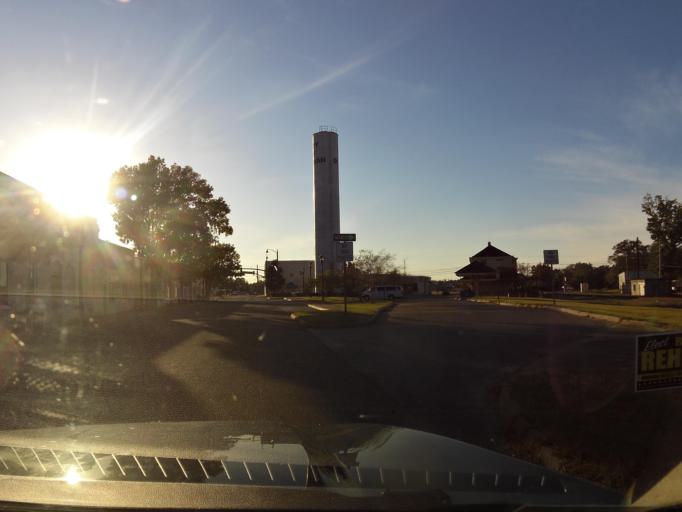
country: US
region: Alabama
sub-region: Houston County
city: Dothan
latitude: 31.2302
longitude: -85.3909
